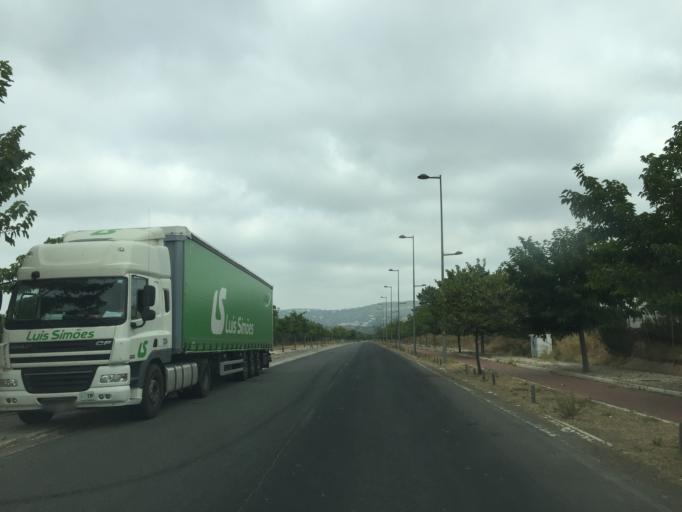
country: PT
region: Faro
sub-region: Faro
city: Santa Barbara de Nexe
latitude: 37.0783
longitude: -7.9760
